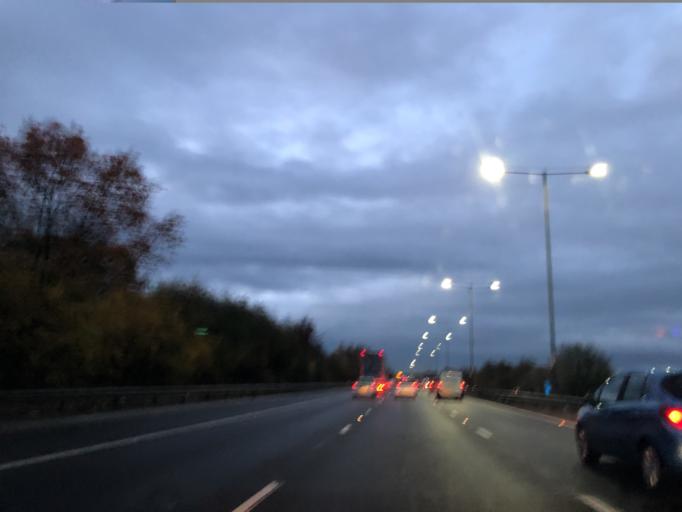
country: GB
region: England
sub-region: Warwickshire
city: Water Orton
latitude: 52.4979
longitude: -1.7376
